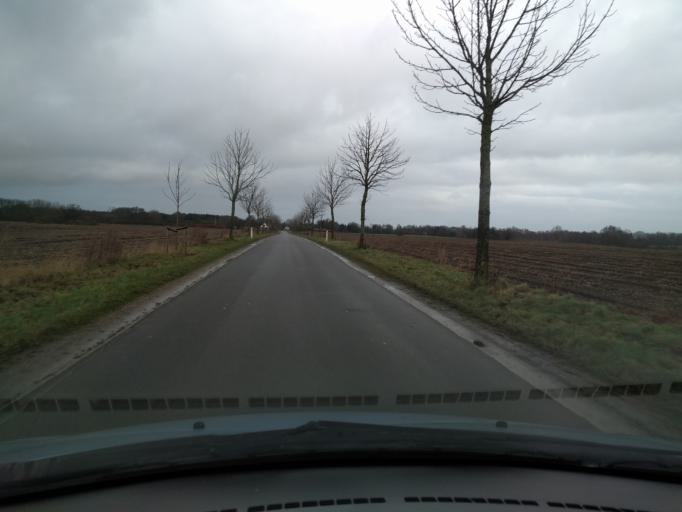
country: DK
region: South Denmark
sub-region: Kerteminde Kommune
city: Langeskov
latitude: 55.3617
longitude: 10.5583
